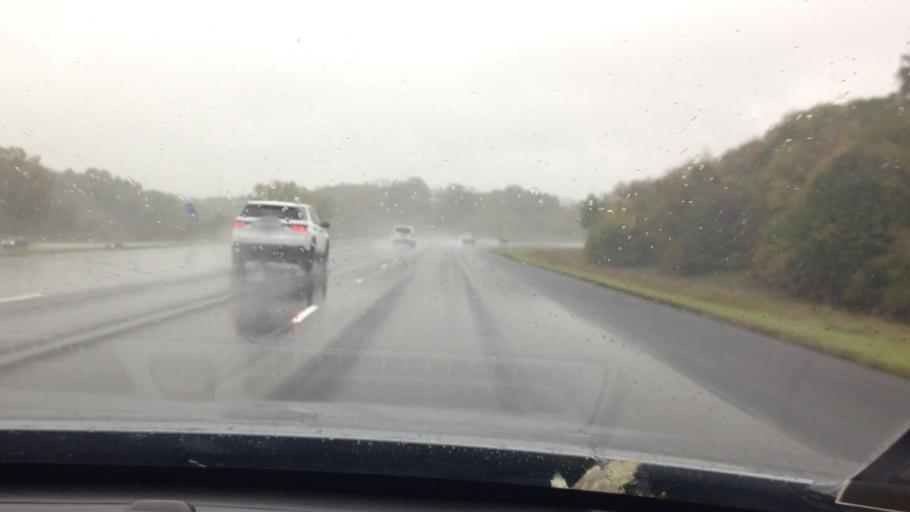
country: US
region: Kansas
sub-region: Wyandotte County
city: Edwardsville
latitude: 39.1660
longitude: -94.8140
